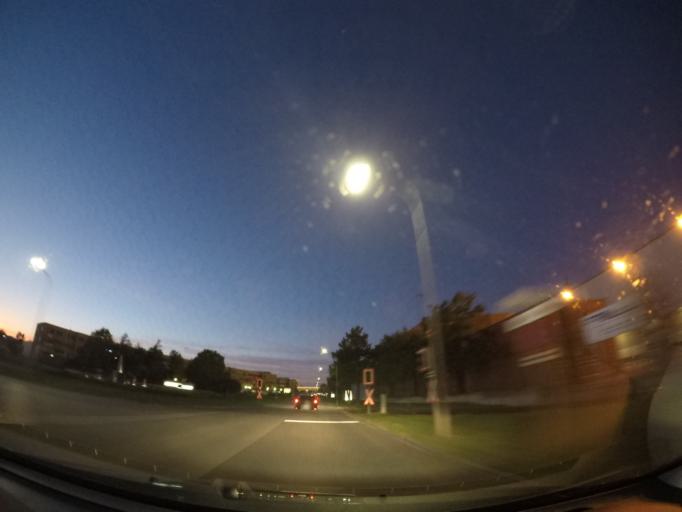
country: AT
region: Lower Austria
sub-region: Politischer Bezirk Modling
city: Laxenburg
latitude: 48.0659
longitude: 16.3366
